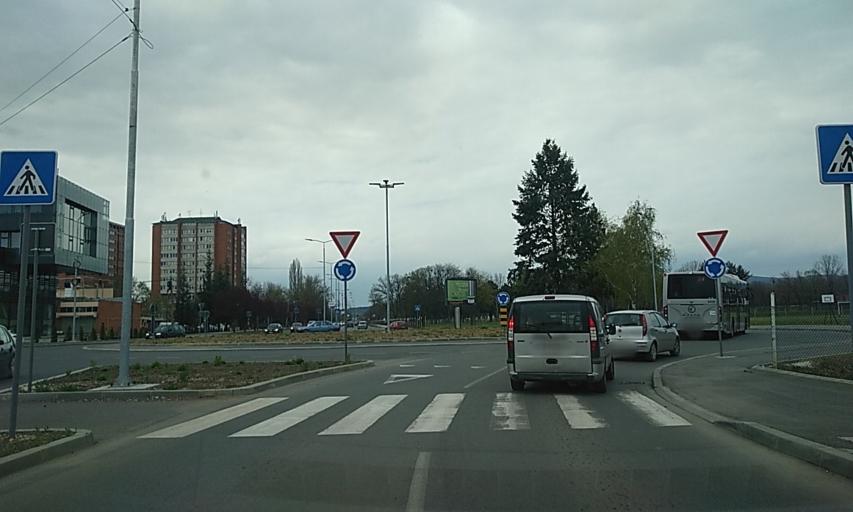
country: RS
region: Central Serbia
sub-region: Nisavski Okrug
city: Nis
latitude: 43.3314
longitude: 21.8959
